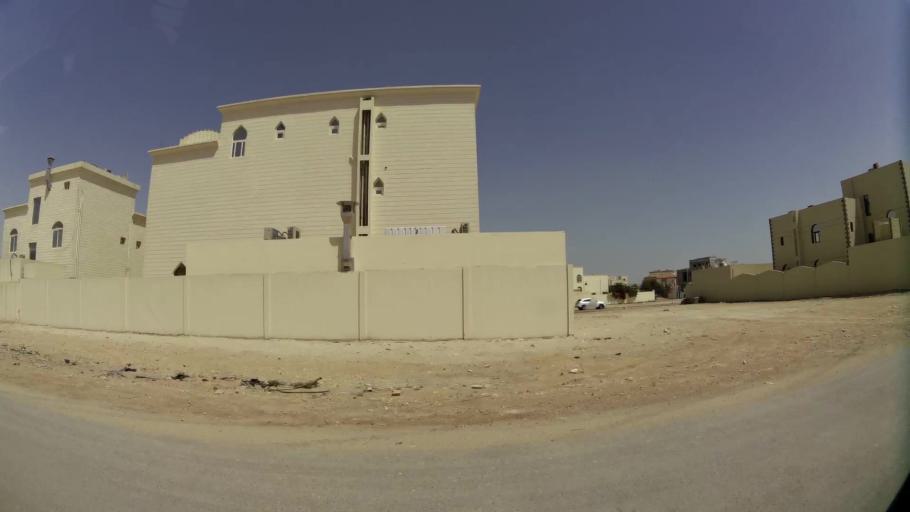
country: QA
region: Baladiyat Umm Salal
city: Umm Salal Muhammad
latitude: 25.3746
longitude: 51.4556
